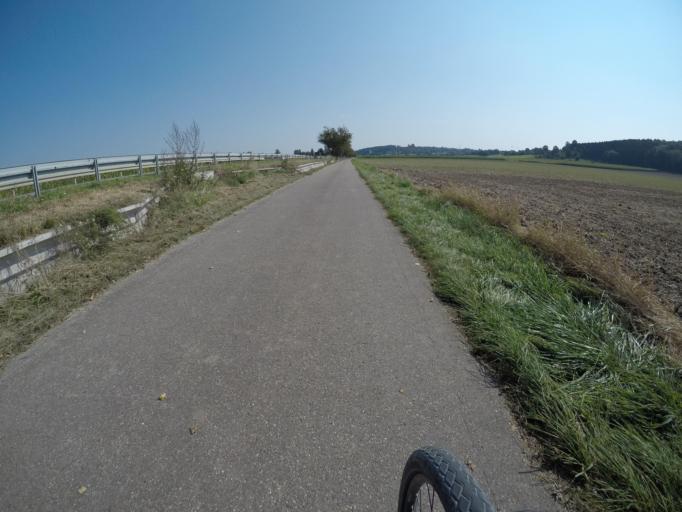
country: DE
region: Bavaria
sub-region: Swabia
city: Aislingen
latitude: 48.5111
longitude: 10.4349
